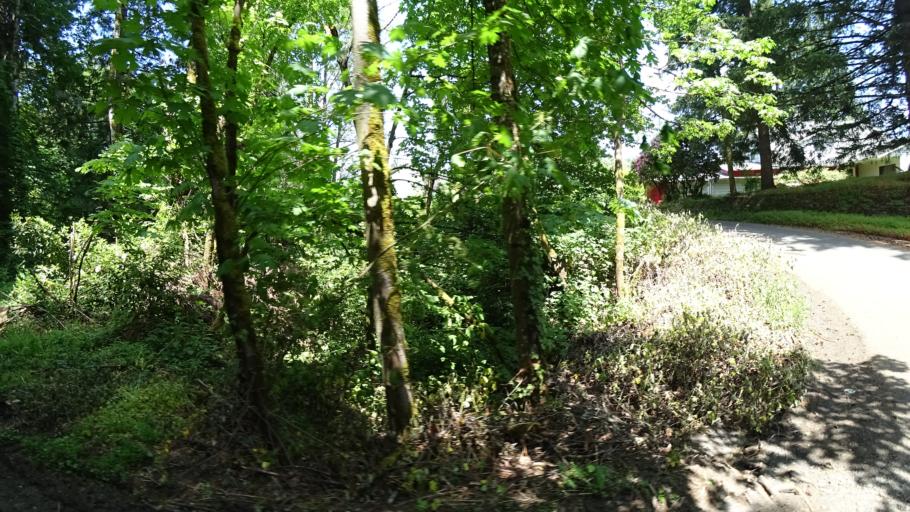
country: US
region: Oregon
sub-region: Clackamas County
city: Happy Valley
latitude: 45.4672
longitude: -122.5078
